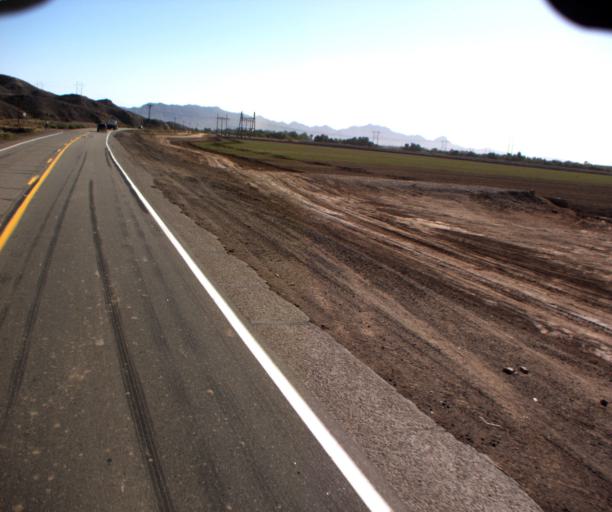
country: US
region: Arizona
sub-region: Yuma County
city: Fortuna Foothills
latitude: 32.7679
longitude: -114.4017
